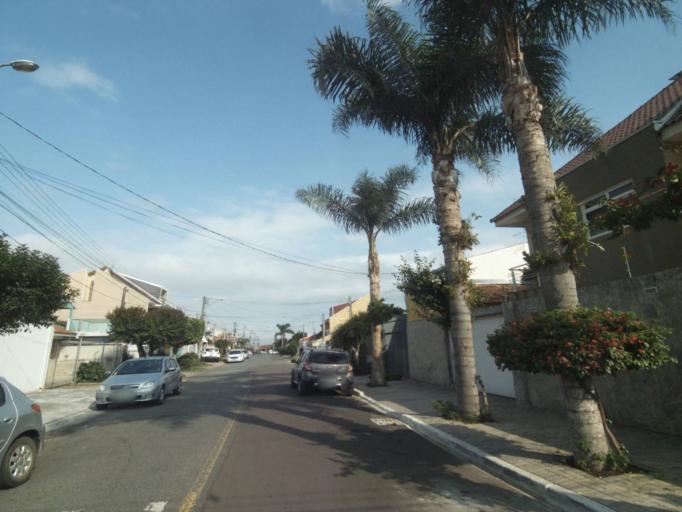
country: BR
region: Parana
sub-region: Sao Jose Dos Pinhais
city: Sao Jose dos Pinhais
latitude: -25.5365
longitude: -49.2600
